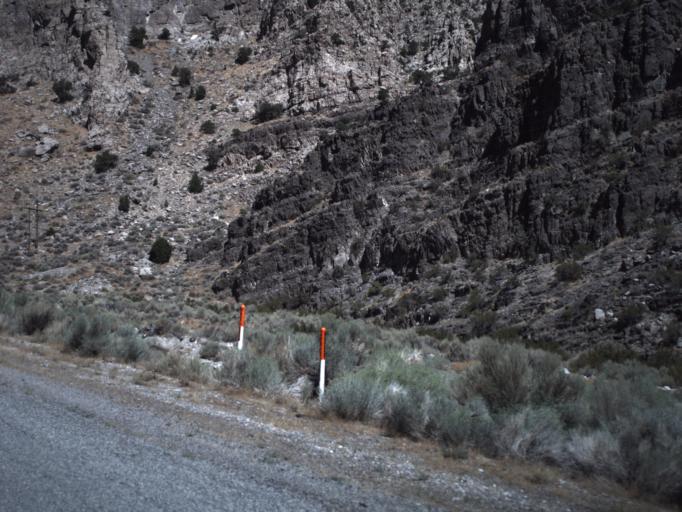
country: US
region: Utah
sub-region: Beaver County
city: Milford
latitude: 39.0872
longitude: -113.5658
